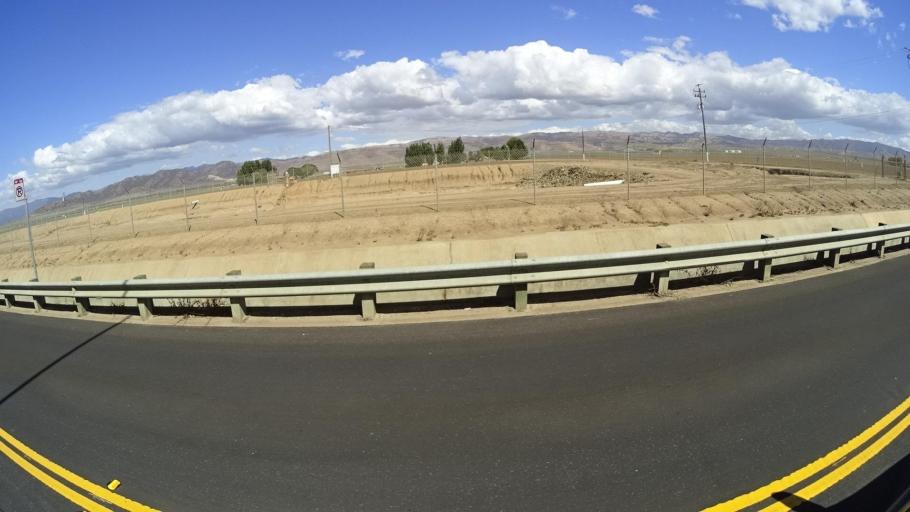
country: US
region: California
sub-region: Monterey County
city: Gonzales
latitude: 36.5248
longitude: -121.4448
